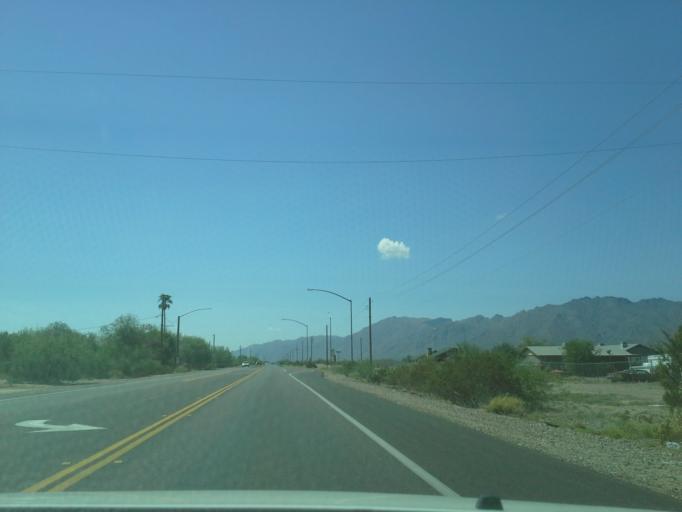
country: US
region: Arizona
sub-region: Maricopa County
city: Laveen
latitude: 33.3148
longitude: -112.1692
